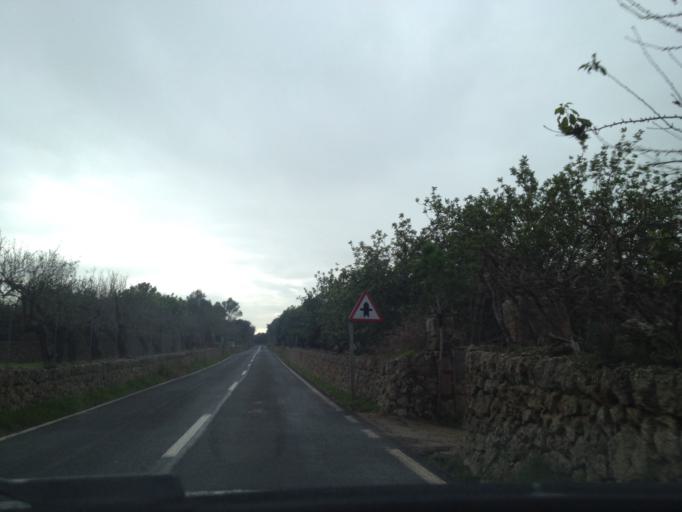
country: ES
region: Balearic Islands
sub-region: Illes Balears
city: Sineu
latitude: 39.6597
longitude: 3.0104
